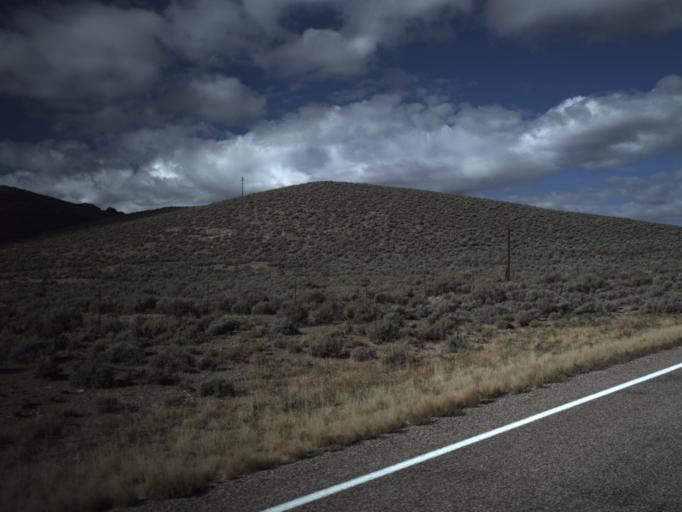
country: US
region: Utah
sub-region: Beaver County
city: Milford
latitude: 38.4229
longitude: -113.1066
